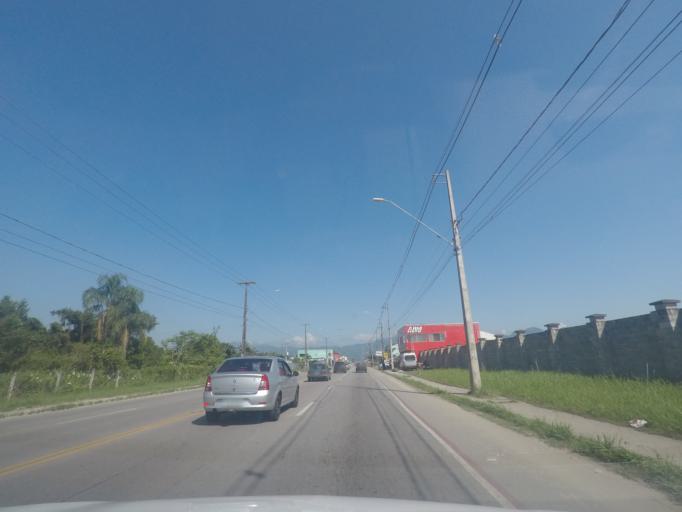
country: BR
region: Parana
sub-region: Paranagua
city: Paranagua
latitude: -25.5617
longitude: -48.5631
